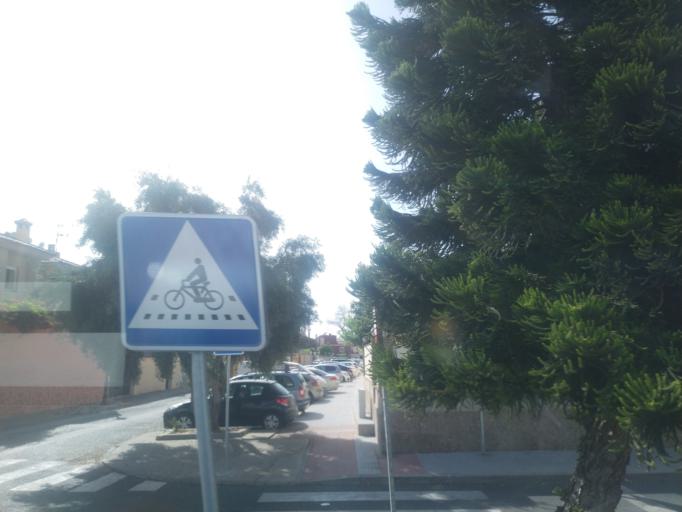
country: ES
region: Andalusia
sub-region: Provincia de Cadiz
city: San Fernando
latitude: 36.4530
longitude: -6.2116
